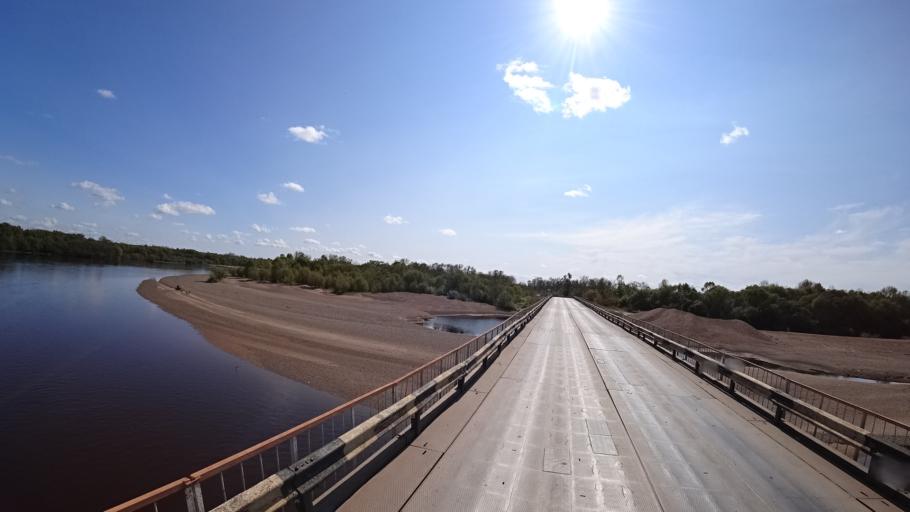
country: RU
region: Amur
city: Arkhara
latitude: 49.3980
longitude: 130.1354
